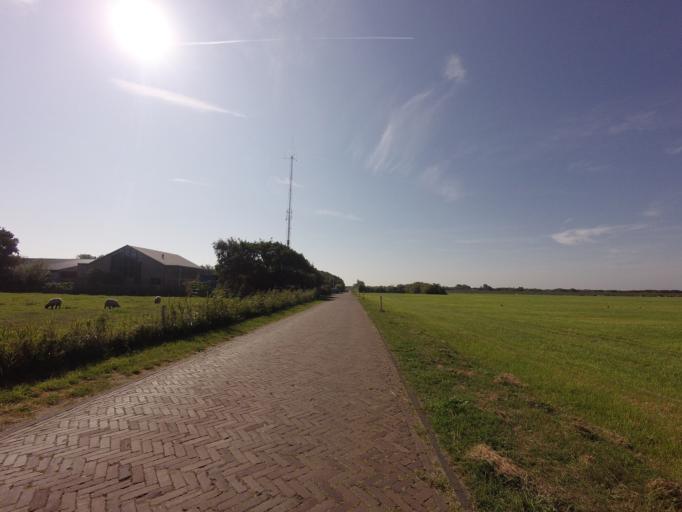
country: NL
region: Friesland
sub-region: Gemeente Schiermonnikoog
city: Schiermonnikoog
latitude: 53.4772
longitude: 6.1544
